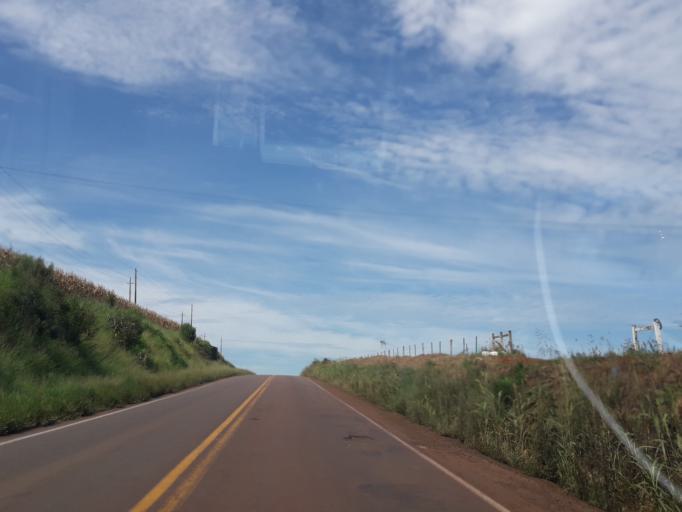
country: AR
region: Misiones
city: Bernardo de Irigoyen
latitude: -26.4116
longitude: -53.5227
